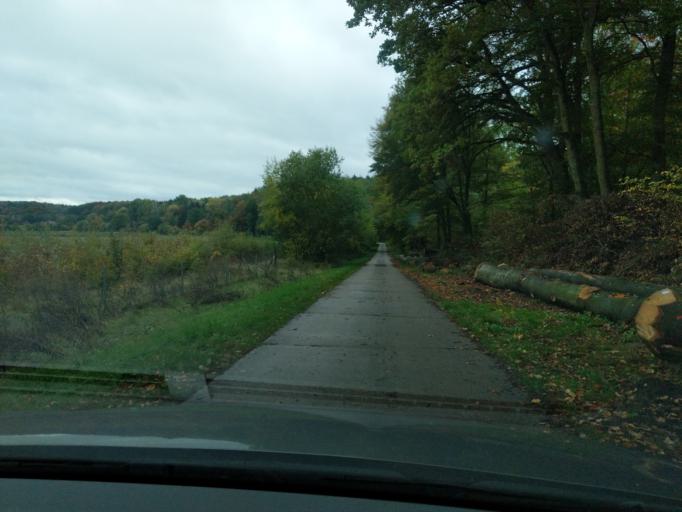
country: DE
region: Schleswig-Holstein
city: Buchhorst
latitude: 53.3958
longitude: 10.5588
